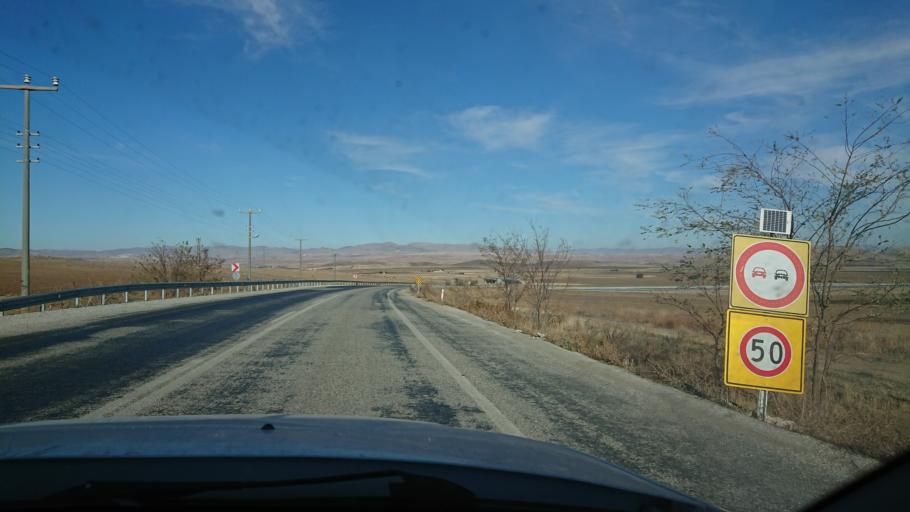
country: TR
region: Aksaray
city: Sariyahsi
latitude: 38.9960
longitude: 33.8503
